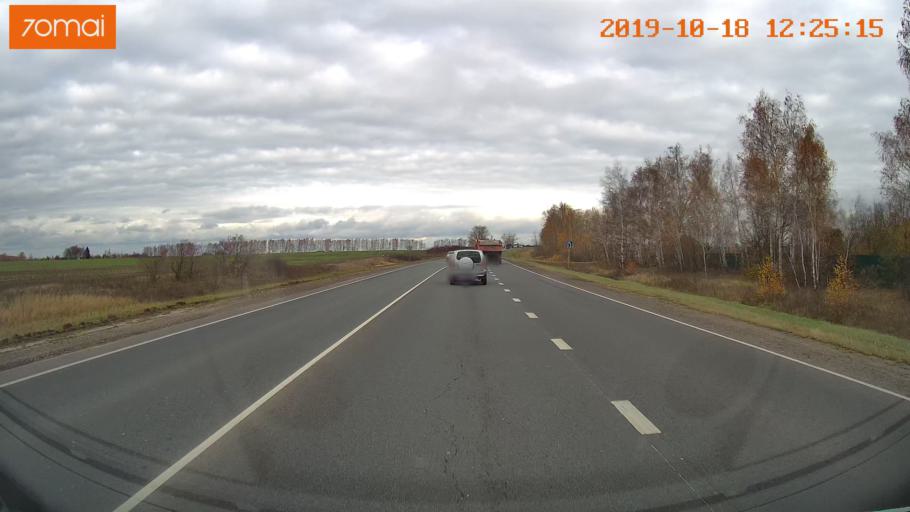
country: RU
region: Rjazan
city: Rybnoye
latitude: 54.5479
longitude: 39.5182
